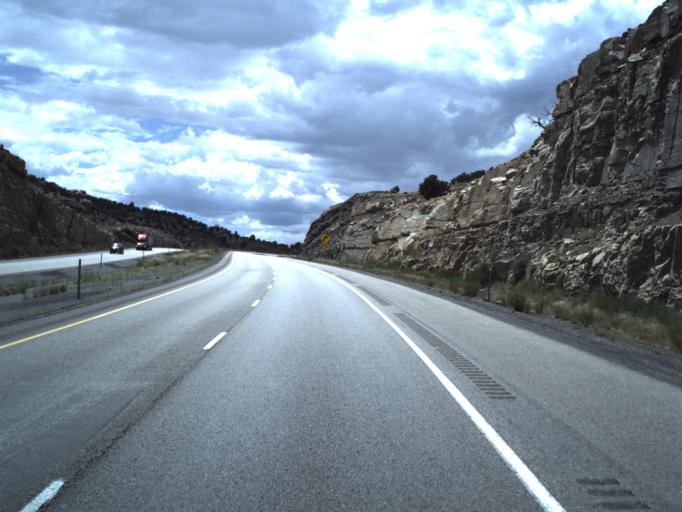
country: US
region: Utah
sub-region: Emery County
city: Ferron
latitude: 38.8038
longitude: -111.2648
